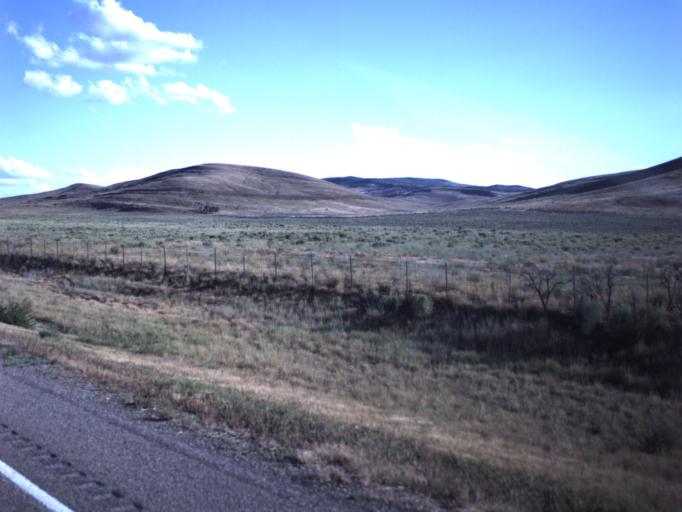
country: US
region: Utah
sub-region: Sanpete County
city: Fairview
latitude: 39.7584
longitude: -111.4817
